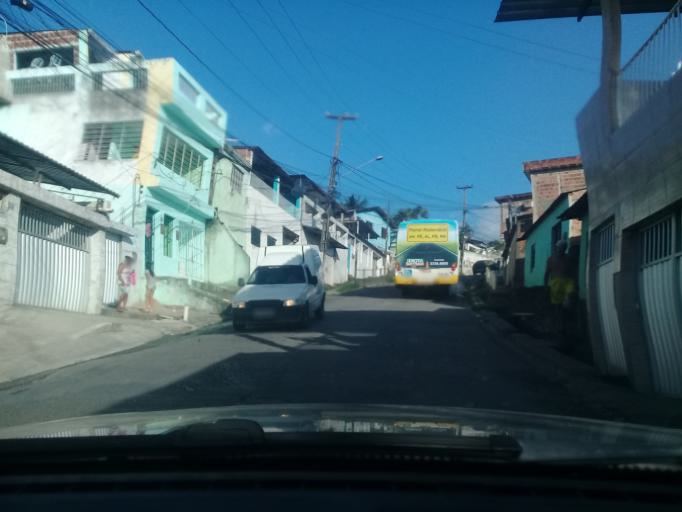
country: BR
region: Pernambuco
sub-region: Jaboatao Dos Guararapes
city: Jaboatao dos Guararapes
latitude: -8.1034
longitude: -34.9646
